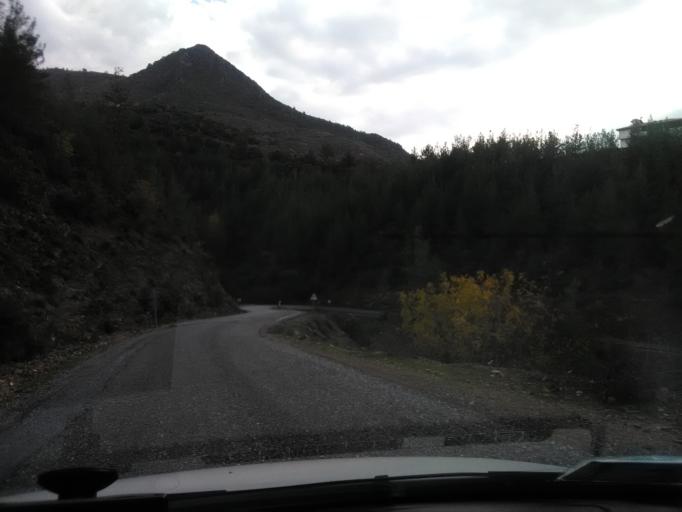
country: TR
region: Antalya
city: Gazipasa
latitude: 36.3024
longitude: 32.3826
